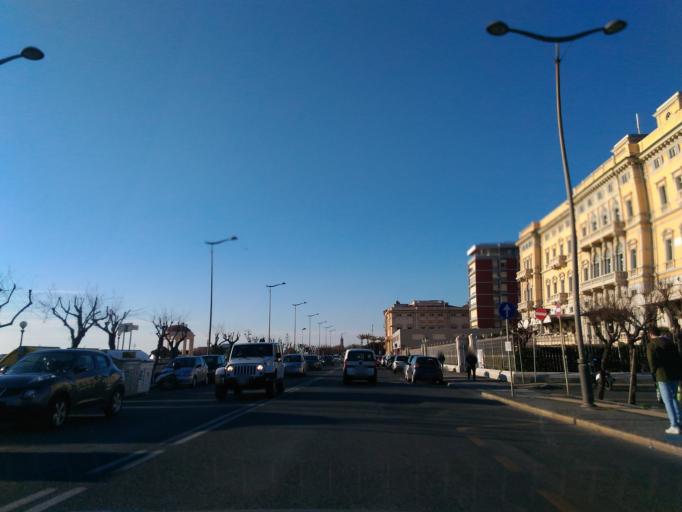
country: IT
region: Tuscany
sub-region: Provincia di Livorno
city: Livorno
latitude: 43.5323
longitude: 10.3027
